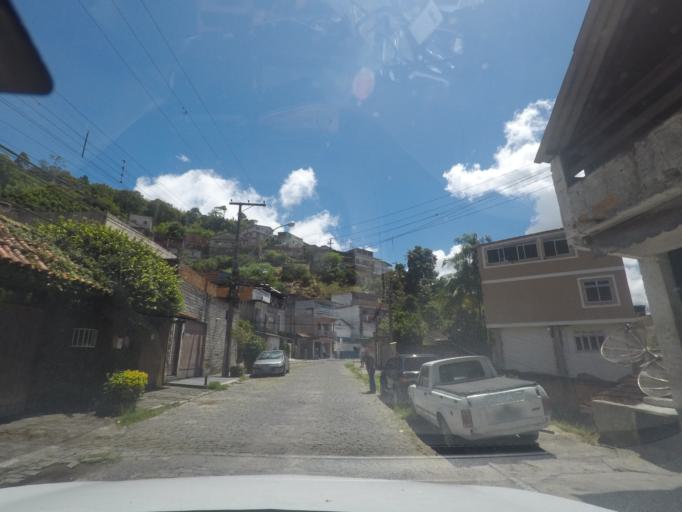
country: BR
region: Rio de Janeiro
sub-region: Teresopolis
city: Teresopolis
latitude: -22.4217
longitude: -42.9860
